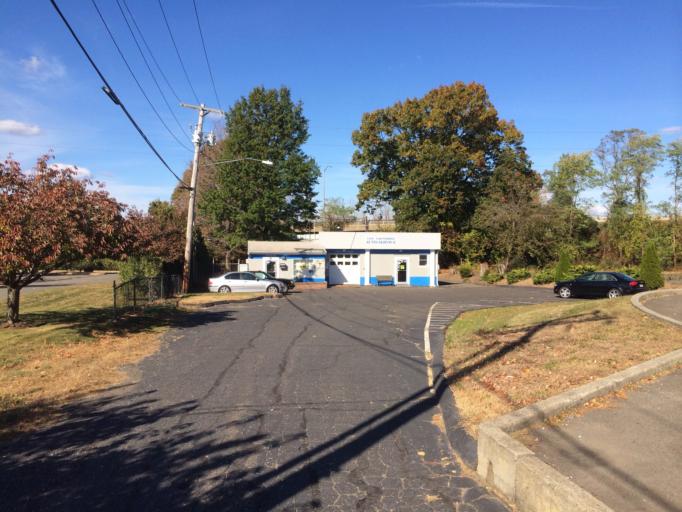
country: US
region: Connecticut
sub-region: New Haven County
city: North Haven
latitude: 41.3980
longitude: -72.8545
